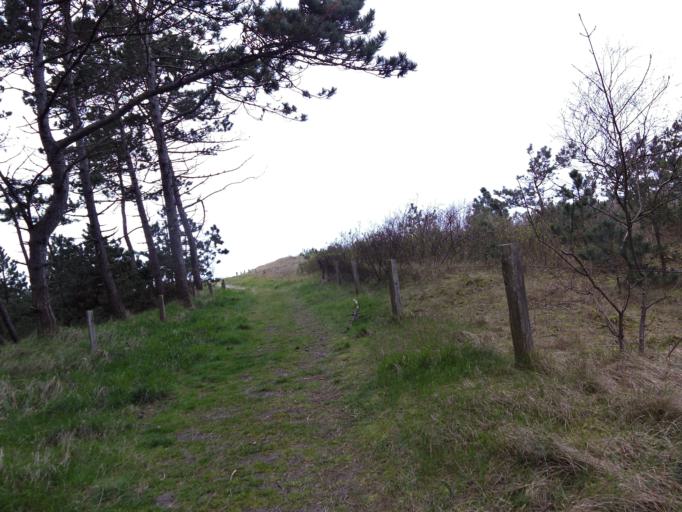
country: DE
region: Mecklenburg-Vorpommern
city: Hiddensee
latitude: 54.5406
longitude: 13.0901
